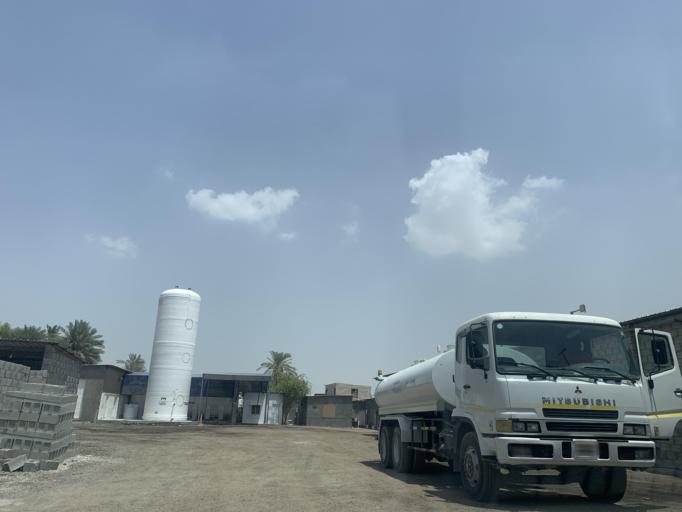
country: BH
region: Central Governorate
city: Madinat Hamad
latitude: 26.1623
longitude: 50.4943
